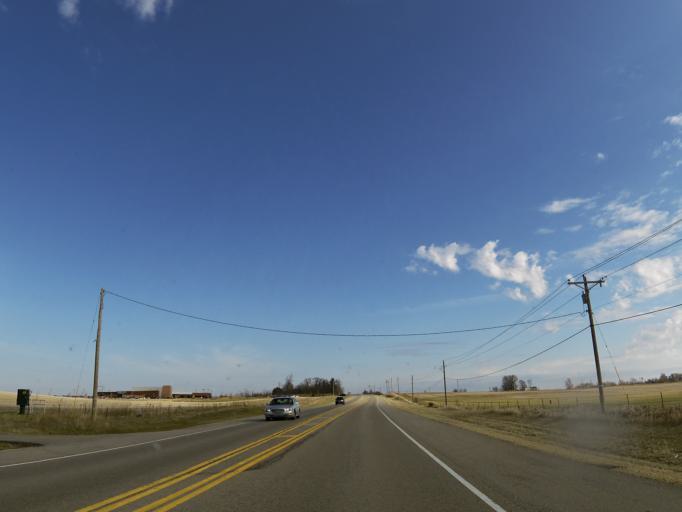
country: US
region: Minnesota
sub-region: Washington County
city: Cottage Grove
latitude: 44.8590
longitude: -92.9033
